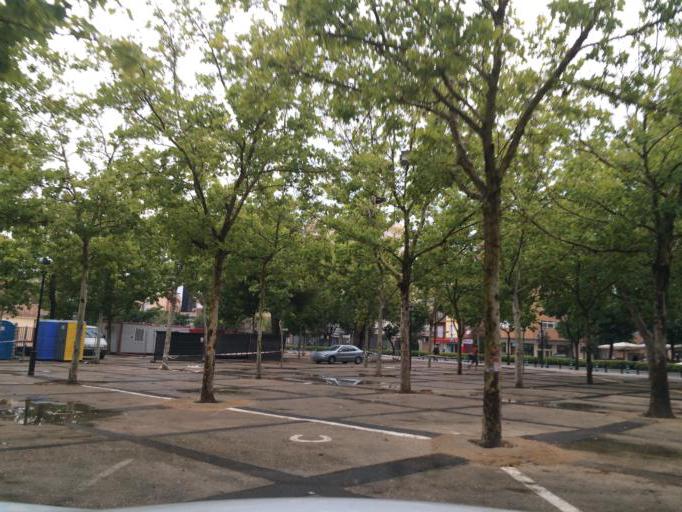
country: ES
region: Castille-La Mancha
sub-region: Provincia de Albacete
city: Albacete
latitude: 38.9961
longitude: -1.8715
